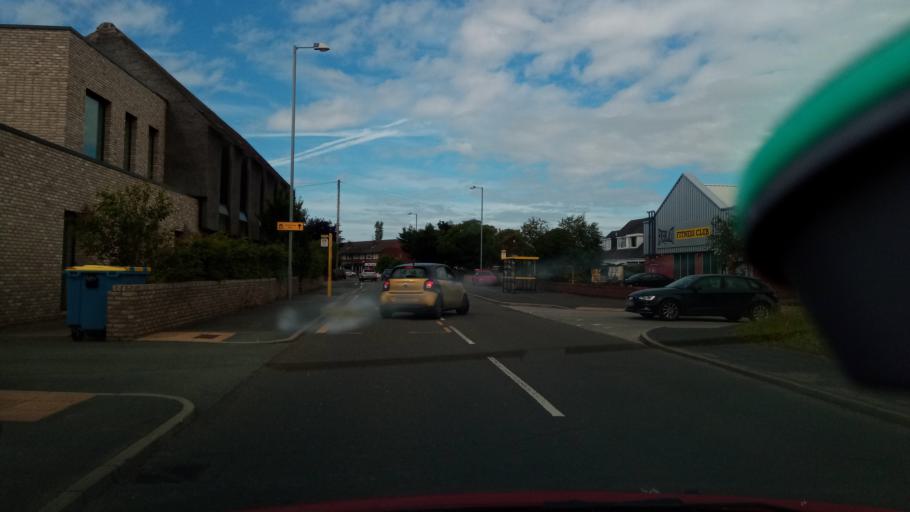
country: GB
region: England
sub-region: Sefton
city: Formby
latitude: 53.5469
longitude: -3.0549
